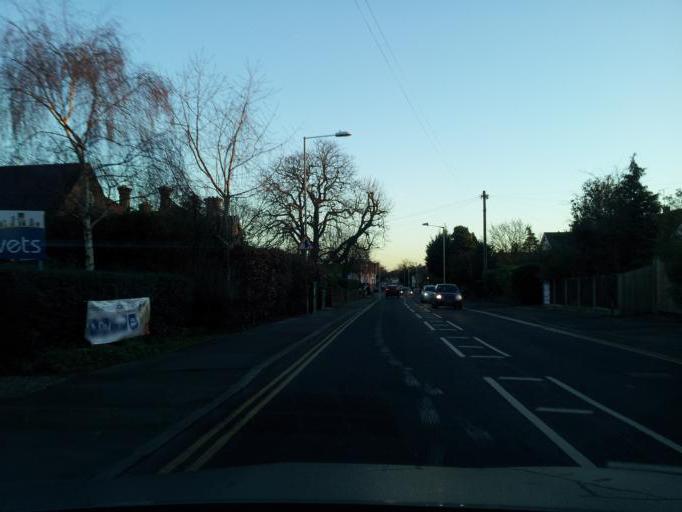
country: GB
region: England
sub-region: Essex
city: Chelmsford
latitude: 51.7421
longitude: 0.4939
